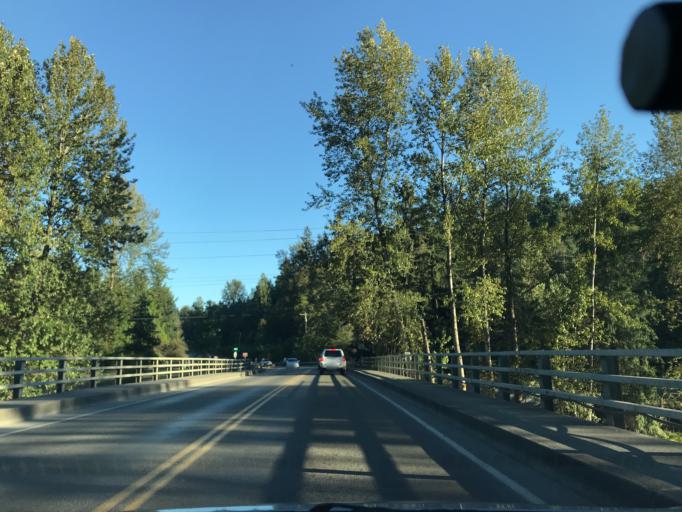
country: US
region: Washington
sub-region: King County
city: Auburn
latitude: 47.2751
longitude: -122.2081
